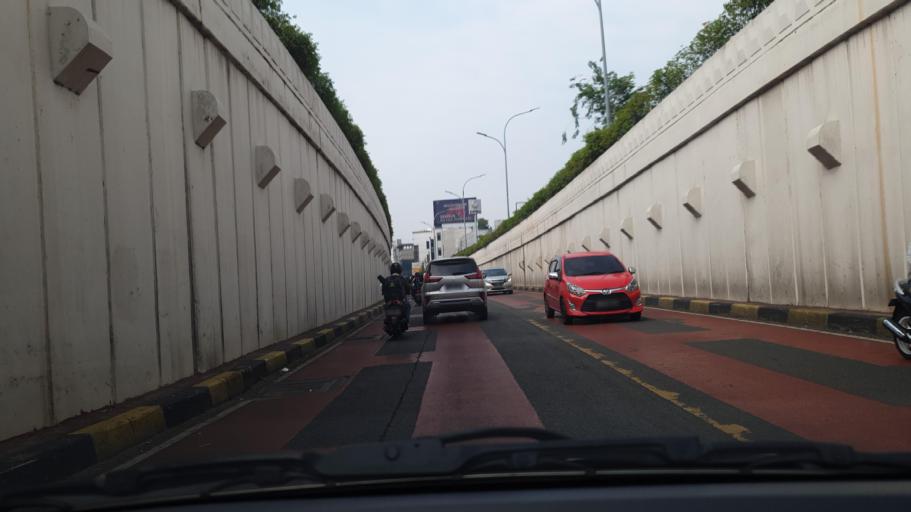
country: ID
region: Jakarta Raya
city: Jakarta
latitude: -6.2481
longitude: 106.7813
